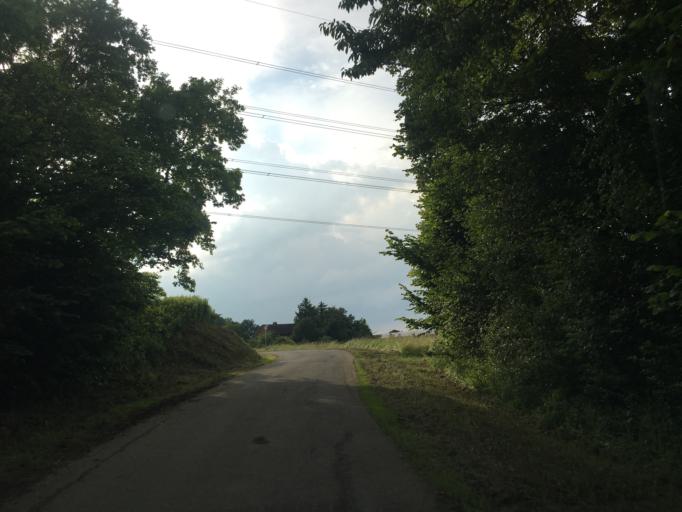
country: DE
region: North Rhine-Westphalia
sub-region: Regierungsbezirk Munster
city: Altenberge
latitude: 52.0268
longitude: 7.5456
